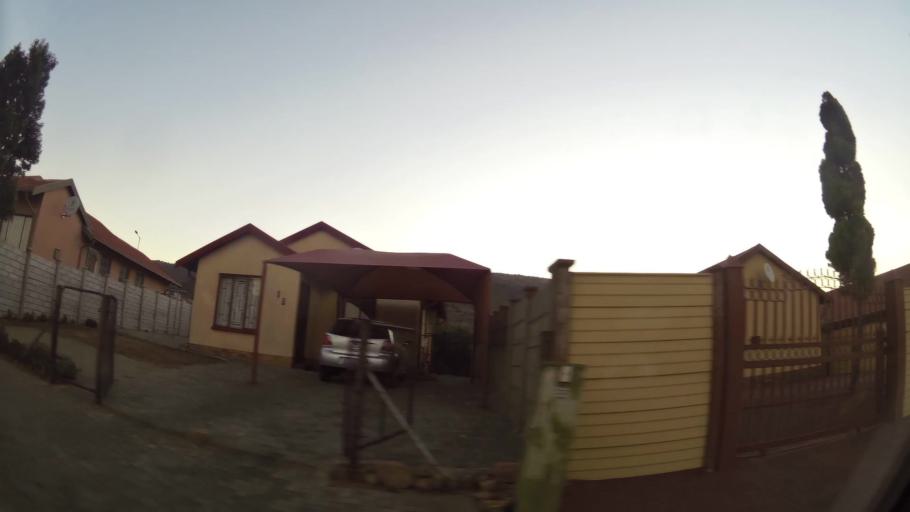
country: ZA
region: North-West
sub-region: Bojanala Platinum District Municipality
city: Rustenburg
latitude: -25.6519
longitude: 27.2023
